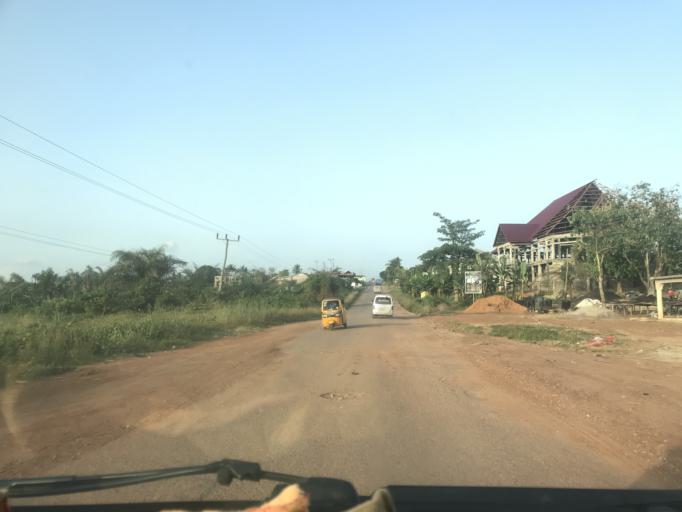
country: GH
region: Ashanti
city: Obuasi
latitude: 6.2027
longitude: -1.6089
